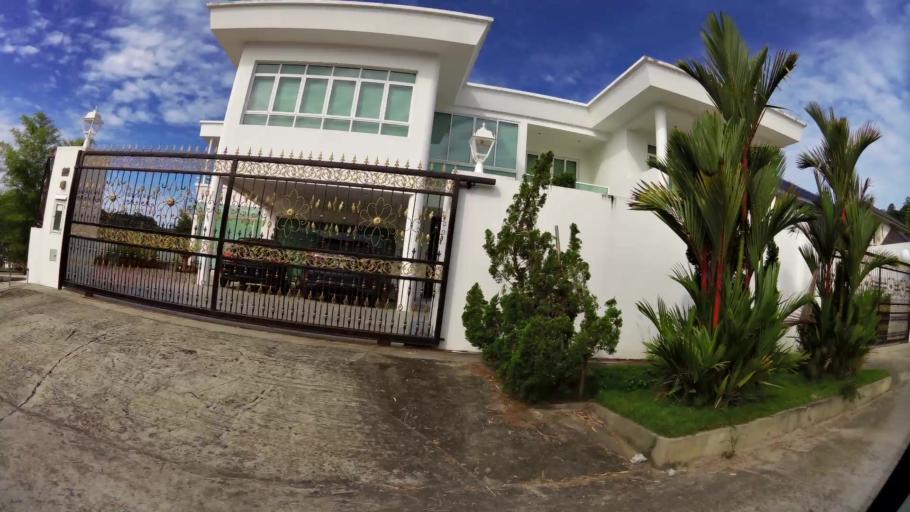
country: BN
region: Brunei and Muara
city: Bandar Seri Begawan
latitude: 4.8978
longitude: 114.9653
